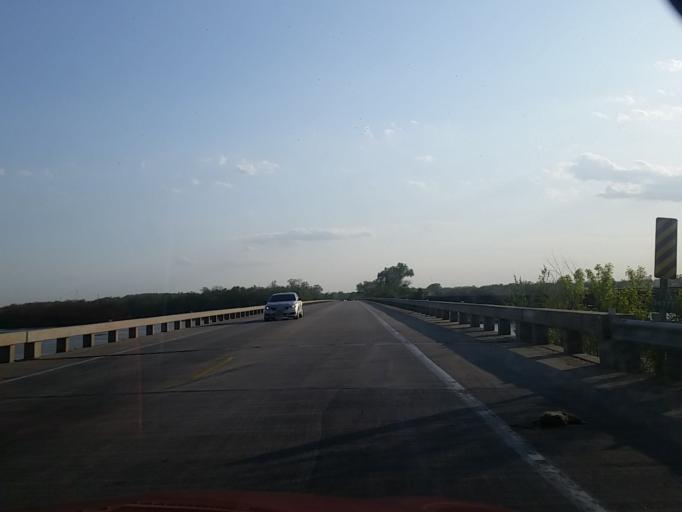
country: US
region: Nebraska
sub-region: Saunders County
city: Ashland
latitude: 41.0624
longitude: -96.3242
